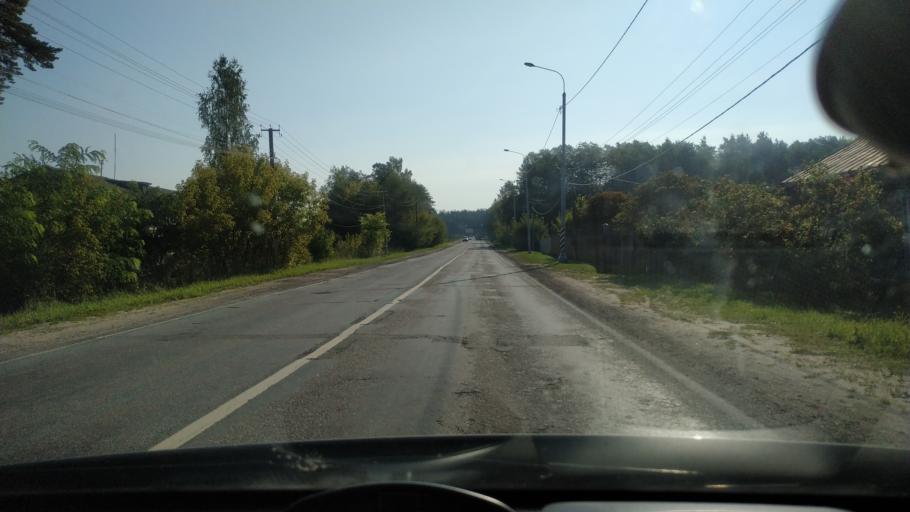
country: RU
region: Moskovskaya
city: Kerva
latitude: 55.5618
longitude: 39.6925
